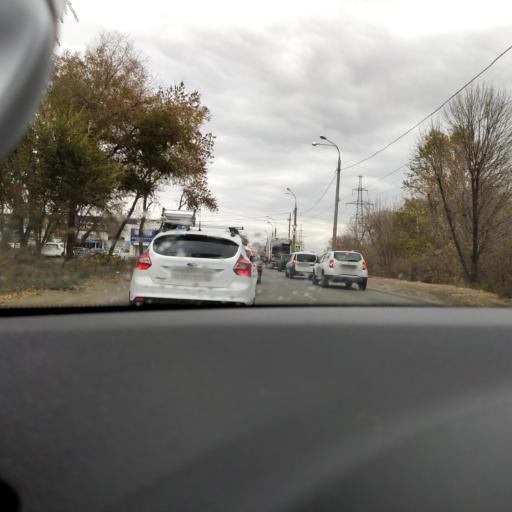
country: RU
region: Samara
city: Smyshlyayevka
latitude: 53.2261
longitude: 50.2987
